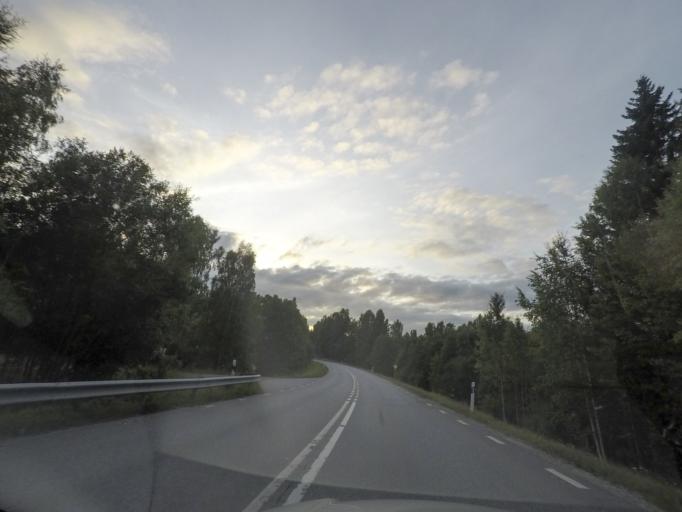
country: SE
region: OErebro
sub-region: Hallefors Kommun
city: Haellefors
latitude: 59.6474
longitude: 14.5977
